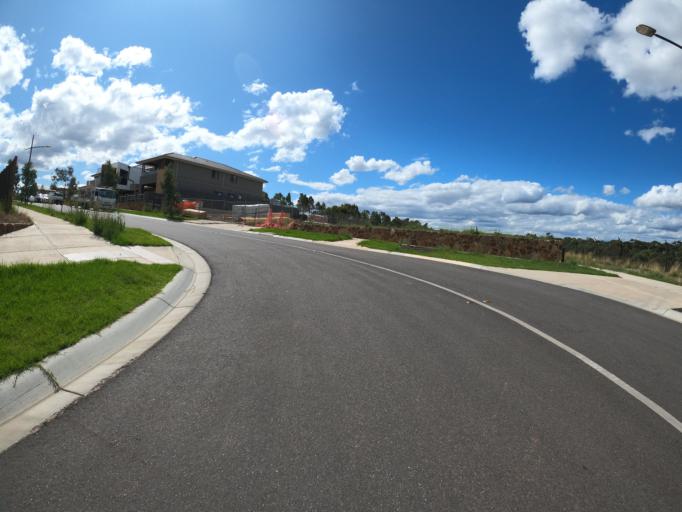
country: AU
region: Victoria
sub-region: Hume
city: Greenvale
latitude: -37.6111
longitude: 144.8918
